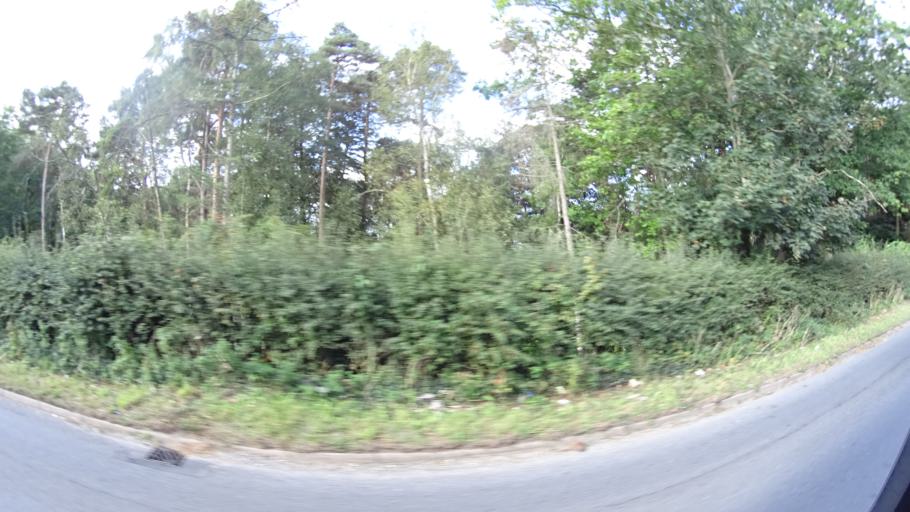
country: GB
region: England
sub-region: Dorset
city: Lytchett Matravers
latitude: 50.7529
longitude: -2.0450
